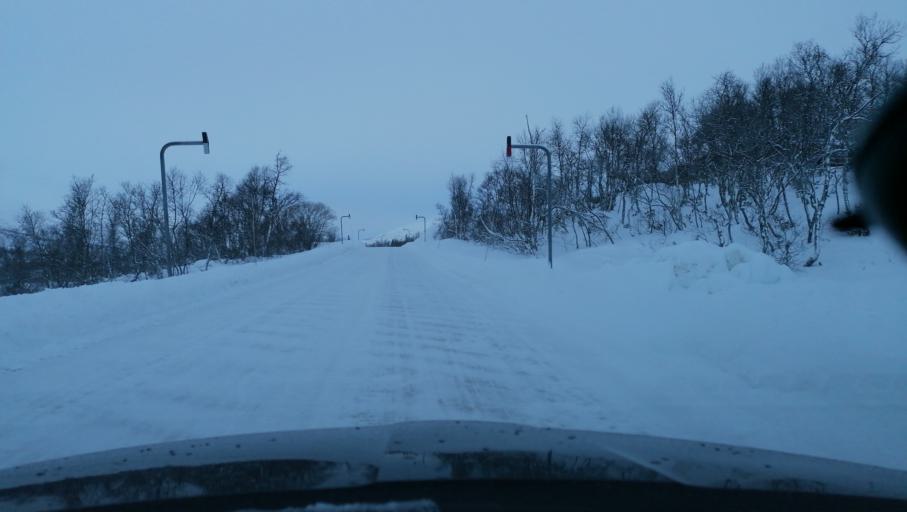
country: NO
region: Aust-Agder
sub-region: Bykle
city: Hovden
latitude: 59.6352
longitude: 7.4538
